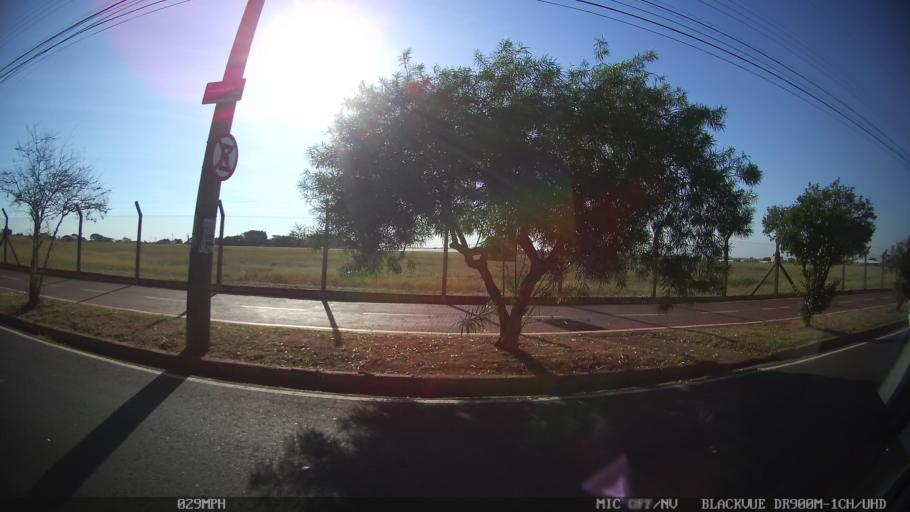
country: BR
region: Sao Paulo
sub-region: Sao Jose Do Rio Preto
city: Sao Jose do Rio Preto
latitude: -20.8155
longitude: -49.4024
